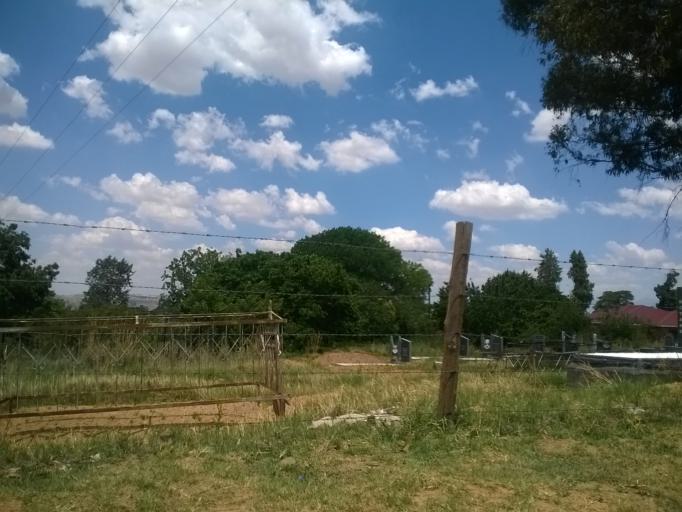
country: LS
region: Berea
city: Teyateyaneng
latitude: -29.1483
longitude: 27.7556
